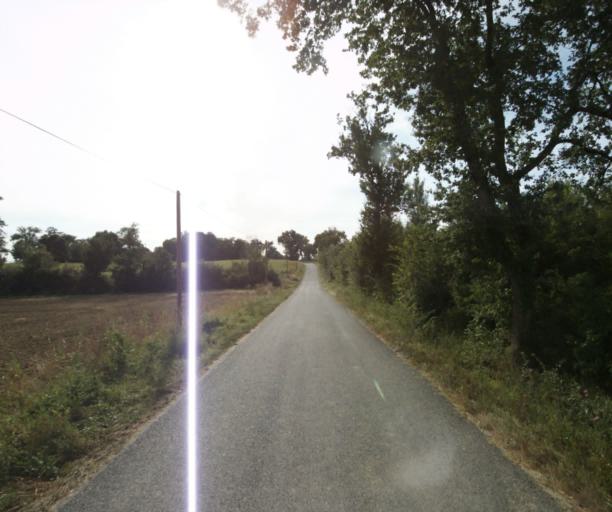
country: FR
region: Midi-Pyrenees
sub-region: Departement du Tarn
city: Puylaurens
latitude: 43.5250
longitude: 2.0367
